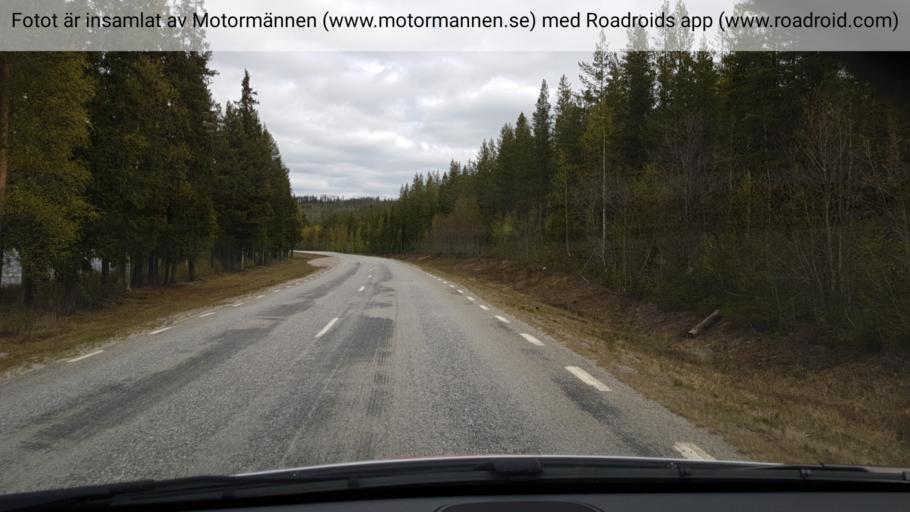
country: SE
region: Vaesterbotten
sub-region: Mala Kommun
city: Mala
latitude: 64.9375
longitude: 18.6245
